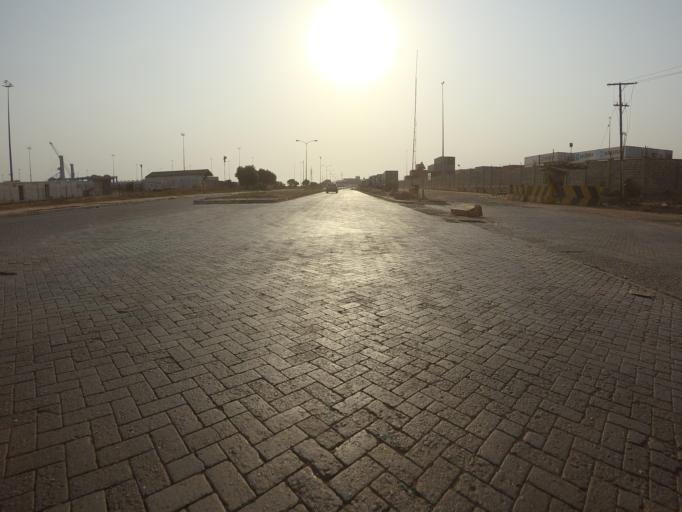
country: GH
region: Greater Accra
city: Tema
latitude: 5.6194
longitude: -0.0162
